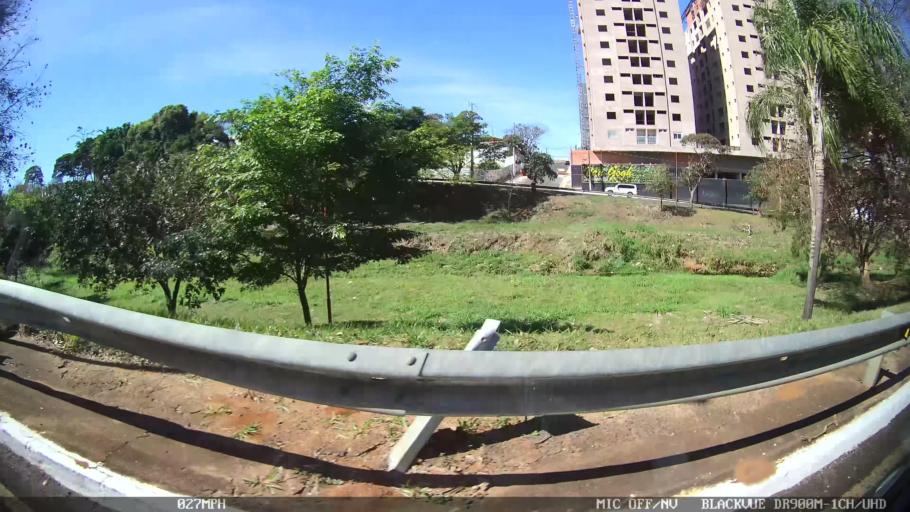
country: BR
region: Sao Paulo
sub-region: Franca
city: Franca
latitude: -20.5502
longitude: -47.4035
